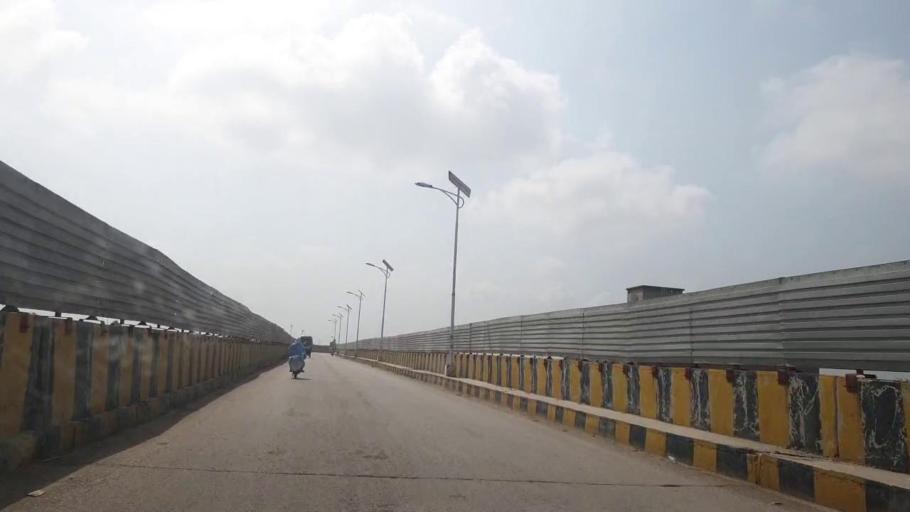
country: PK
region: Sindh
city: Khairpur
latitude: 27.5284
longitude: 68.7420
